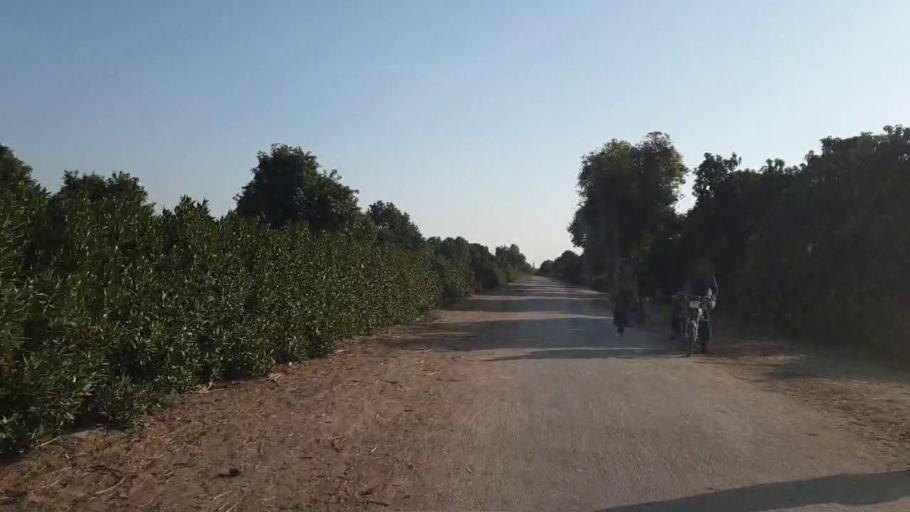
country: PK
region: Sindh
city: Tando Allahyar
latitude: 25.3661
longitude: 68.6825
